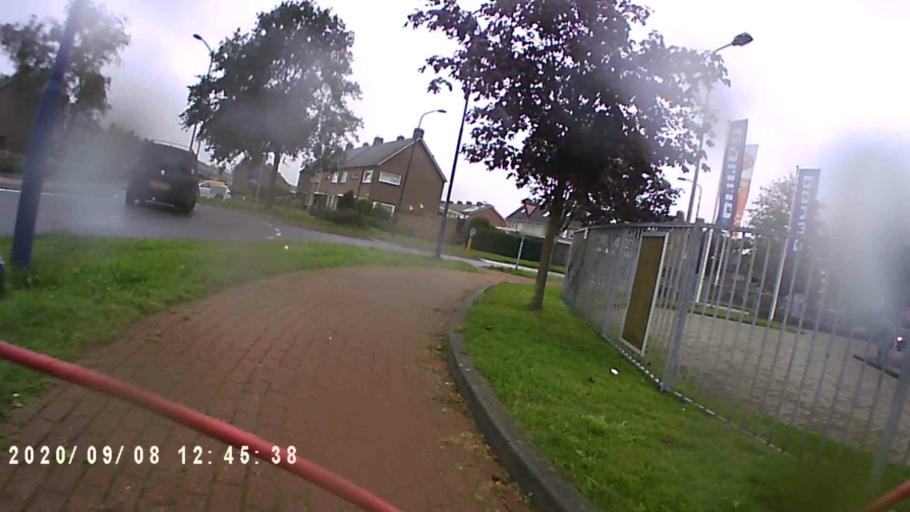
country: NL
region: Groningen
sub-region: Gemeente Veendam
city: Veendam
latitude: 53.1096
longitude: 6.8895
